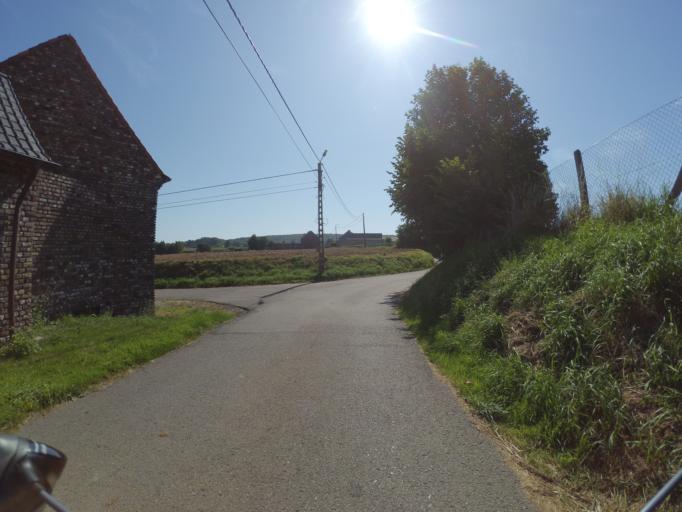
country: BE
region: Flanders
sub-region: Provincie Oost-Vlaanderen
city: Ronse
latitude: 50.7712
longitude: 3.6232
